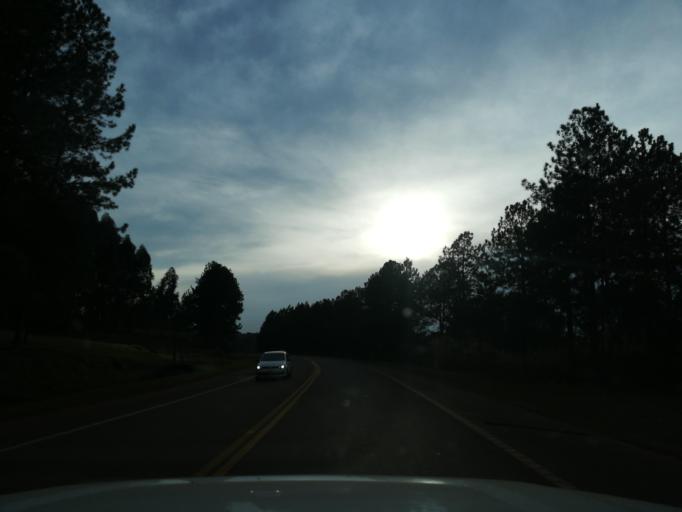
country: AR
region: Misiones
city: San Vicente
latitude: -26.6360
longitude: -54.1276
